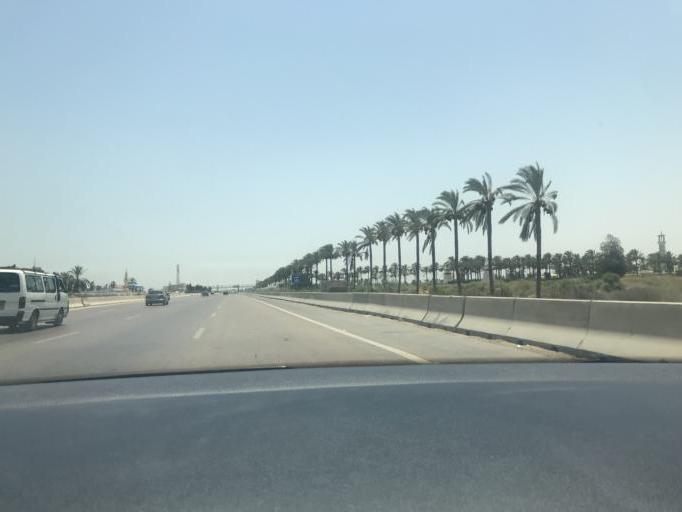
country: EG
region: Al Buhayrah
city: Abu al Matamir
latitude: 30.9129
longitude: 29.8650
